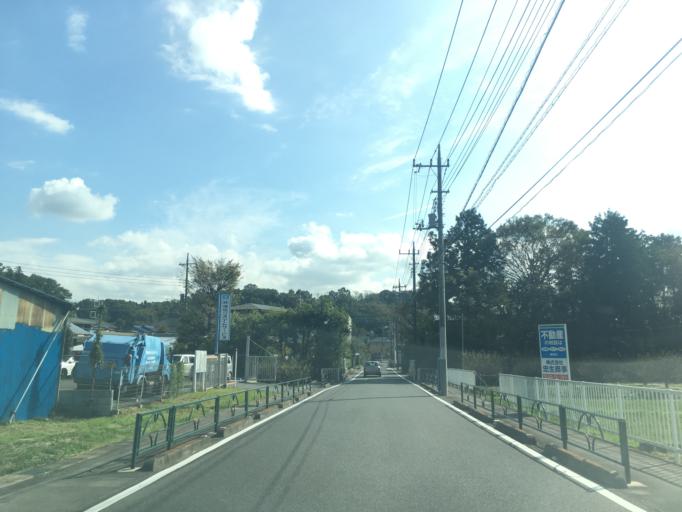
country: JP
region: Tokyo
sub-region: Machida-shi
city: Machida
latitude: 35.5970
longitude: 139.4090
